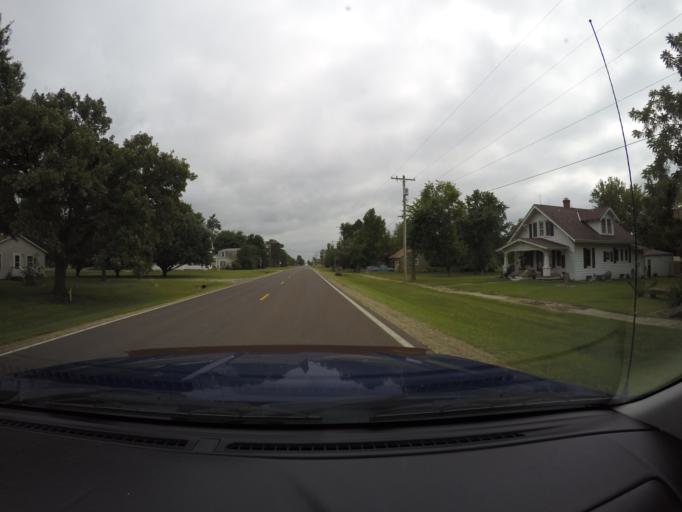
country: US
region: Kansas
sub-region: Morris County
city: Council Grove
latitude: 38.8467
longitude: -96.5940
